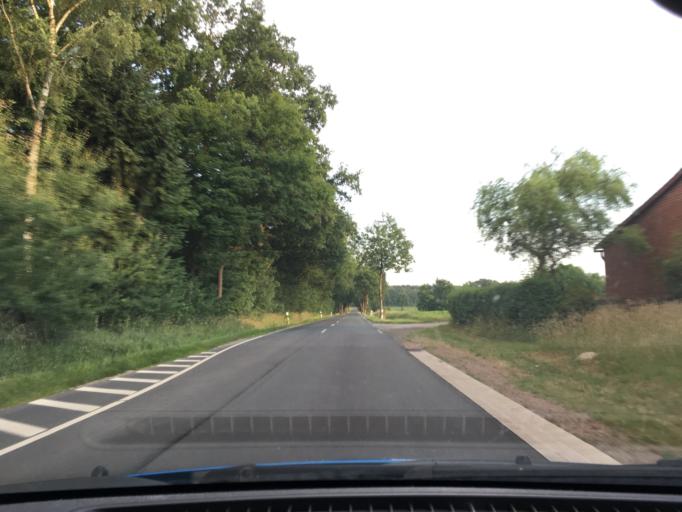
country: DE
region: Lower Saxony
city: Scharnhorst
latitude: 52.7153
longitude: 10.3172
